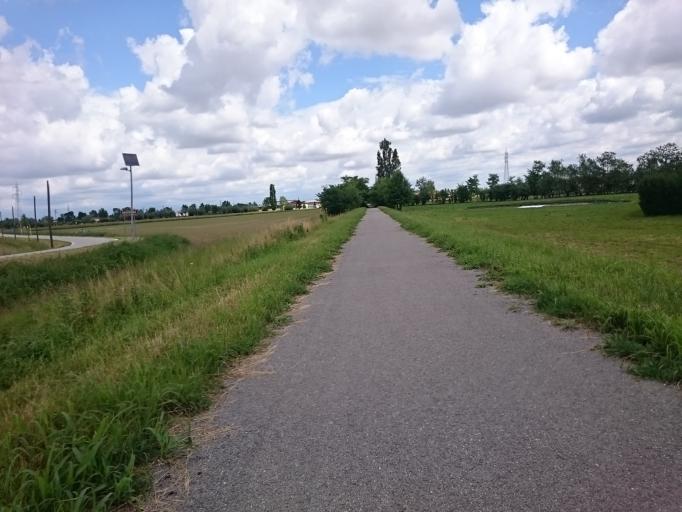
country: IT
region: Veneto
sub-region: Provincia di Padova
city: Piazzola sul Brenta
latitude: 45.5213
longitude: 11.7618
